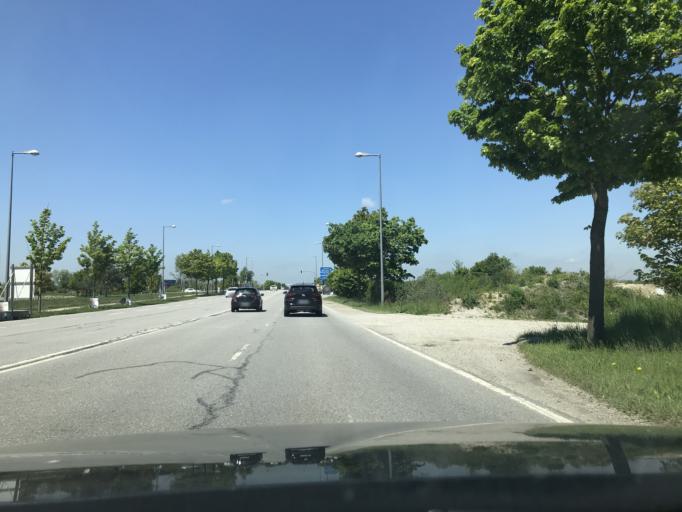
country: DE
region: Bavaria
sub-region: Upper Bavaria
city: Feldkirchen
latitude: 48.1403
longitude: 11.7118
